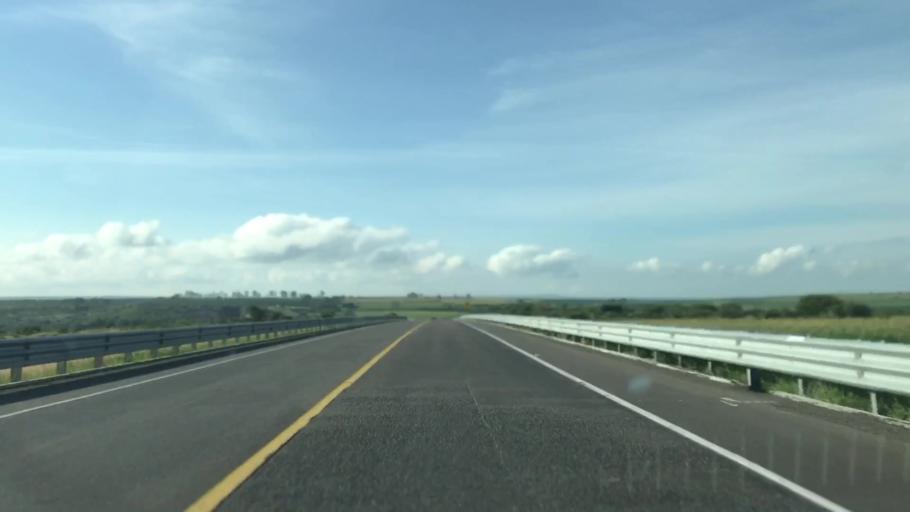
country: MX
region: Jalisco
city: Encarnacion de Diaz
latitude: 21.4282
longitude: -102.2049
